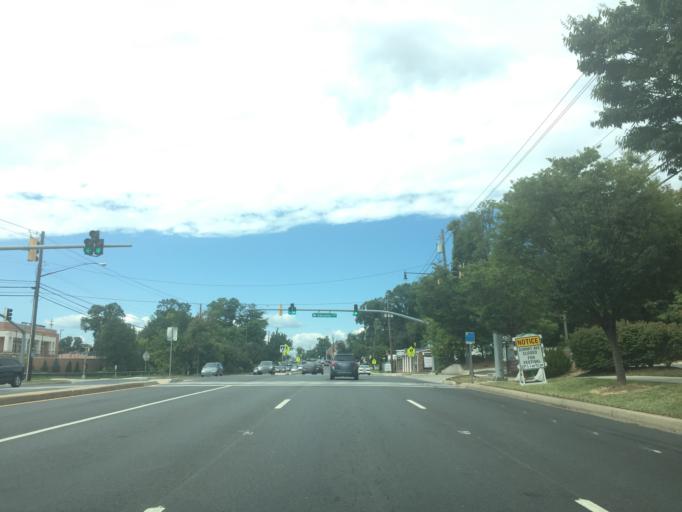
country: US
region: Maryland
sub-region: Montgomery County
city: Gaithersburg
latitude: 39.1355
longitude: -77.1918
